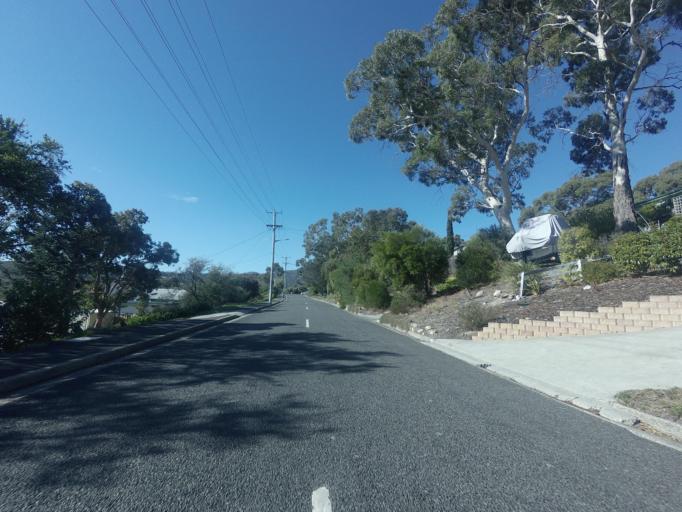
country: AU
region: Tasmania
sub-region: Clarence
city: Lindisfarne
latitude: -42.8416
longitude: 147.3427
